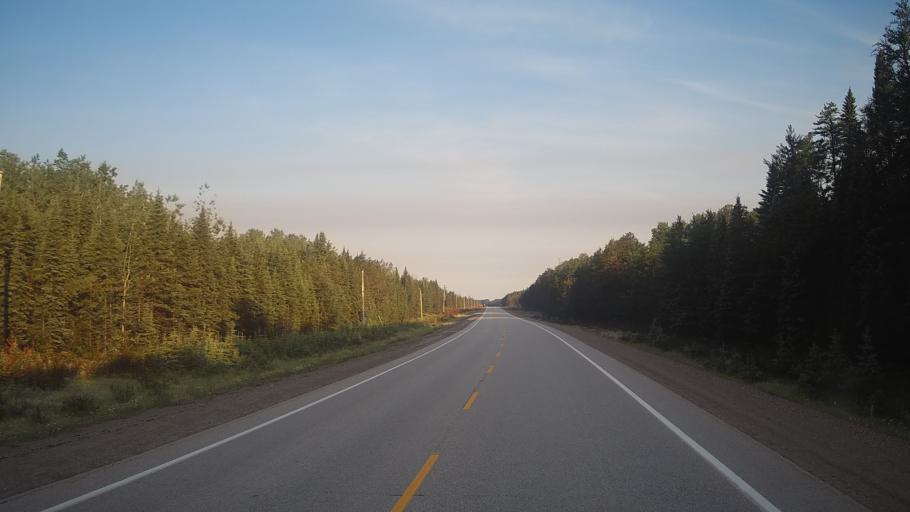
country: CA
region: Ontario
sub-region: Rainy River District
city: Atikokan
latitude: 49.2462
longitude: -91.0358
